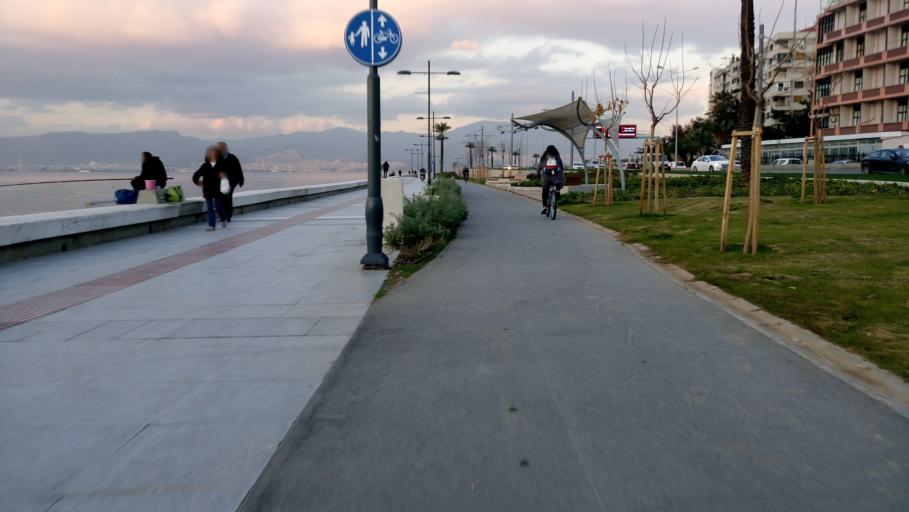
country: TR
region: Izmir
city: Izmir
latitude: 38.4122
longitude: 27.1204
